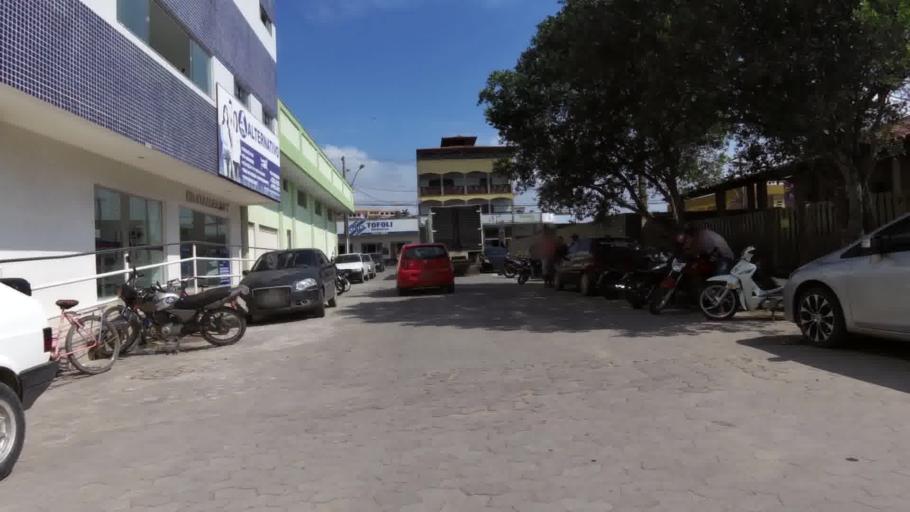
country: BR
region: Espirito Santo
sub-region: Marataizes
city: Marataizes
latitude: -21.0289
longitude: -40.8167
